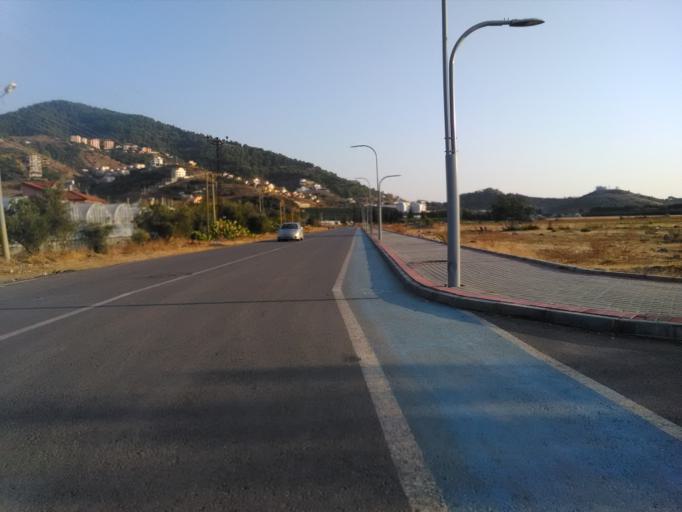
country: TR
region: Antalya
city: Gazipasa
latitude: 36.2444
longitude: 32.2971
